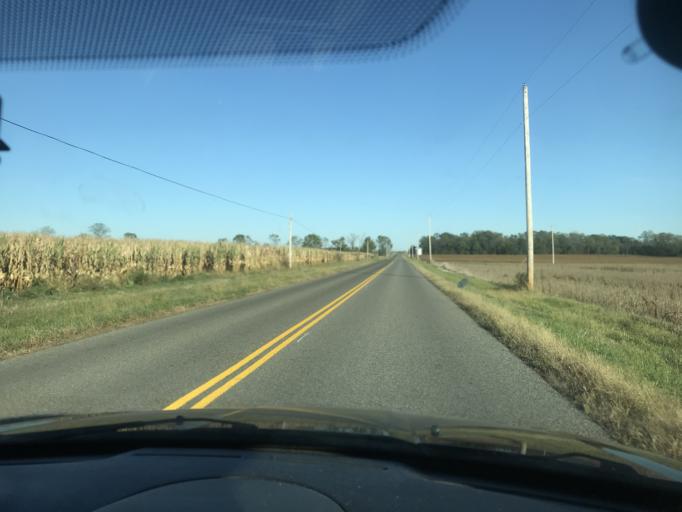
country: US
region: Ohio
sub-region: Logan County
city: Bellefontaine
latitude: 40.3213
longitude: -83.8240
